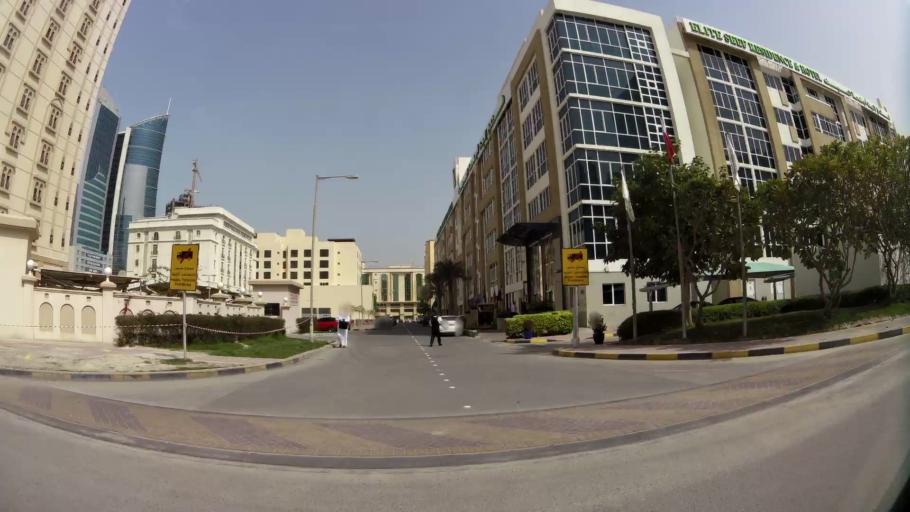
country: BH
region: Manama
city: Jidd Hafs
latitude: 26.2389
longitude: 50.5380
